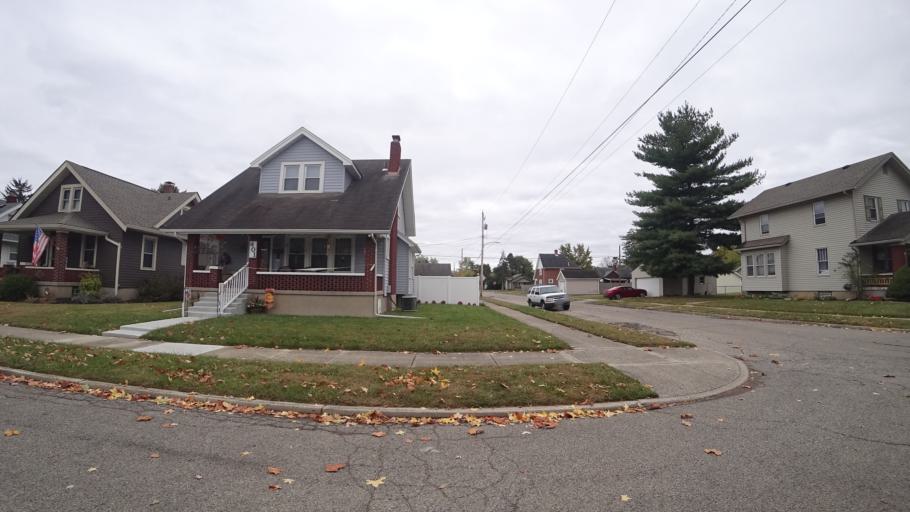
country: US
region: Ohio
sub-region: Butler County
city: Fairfield
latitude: 39.3661
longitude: -84.5606
